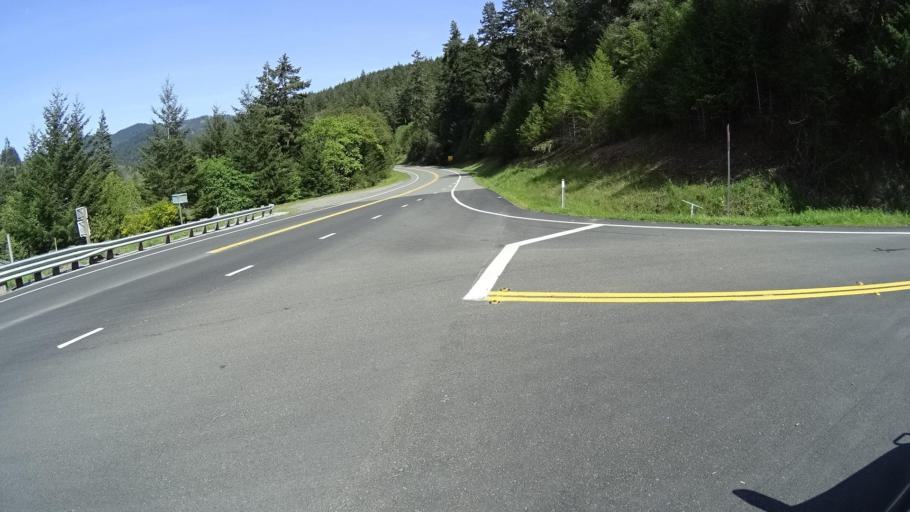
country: US
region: California
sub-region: Humboldt County
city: Hydesville
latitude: 40.4684
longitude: -123.7994
